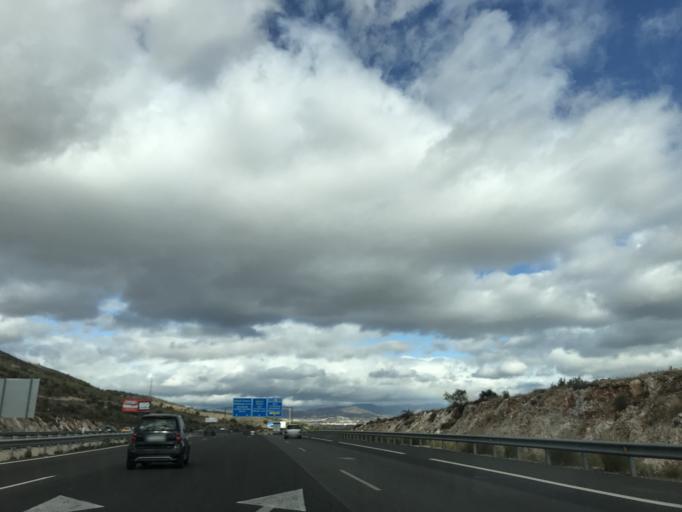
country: ES
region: Andalusia
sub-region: Provincia de Malaga
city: Torremolinos
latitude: 36.6210
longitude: -4.5169
